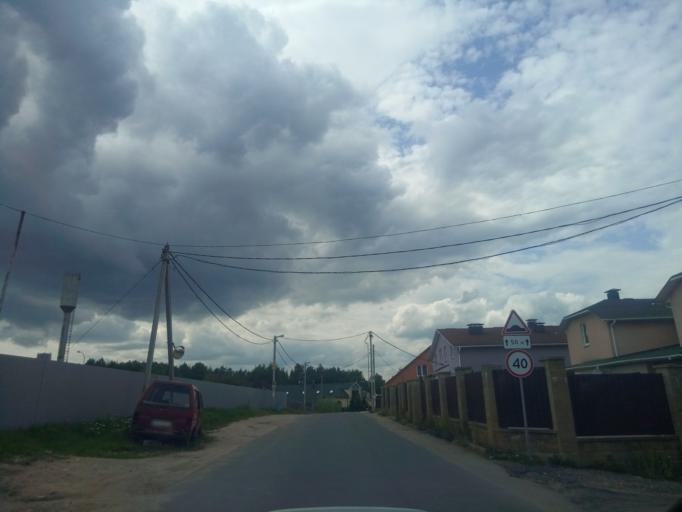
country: BY
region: Minsk
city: Zhdanovichy
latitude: 53.9375
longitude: 27.4228
